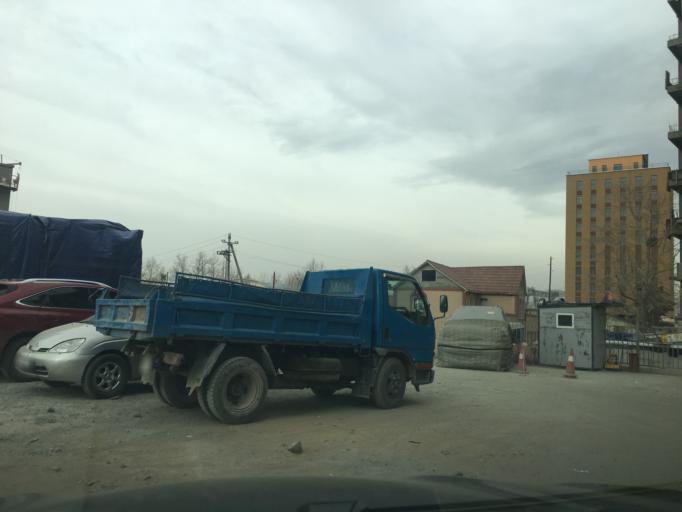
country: MN
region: Ulaanbaatar
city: Ulaanbaatar
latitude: 47.9037
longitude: 106.8820
